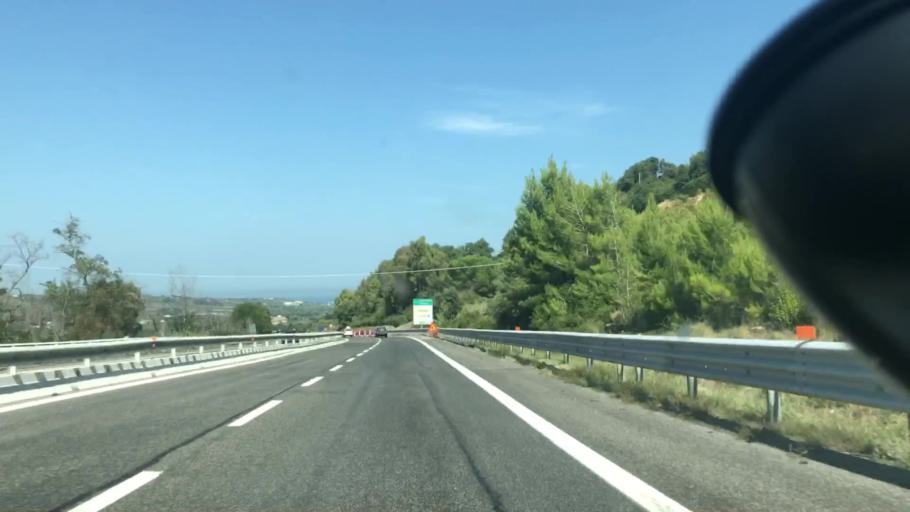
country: IT
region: Abruzzo
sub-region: Provincia di Chieti
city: Vasto
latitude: 42.1451
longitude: 14.6564
